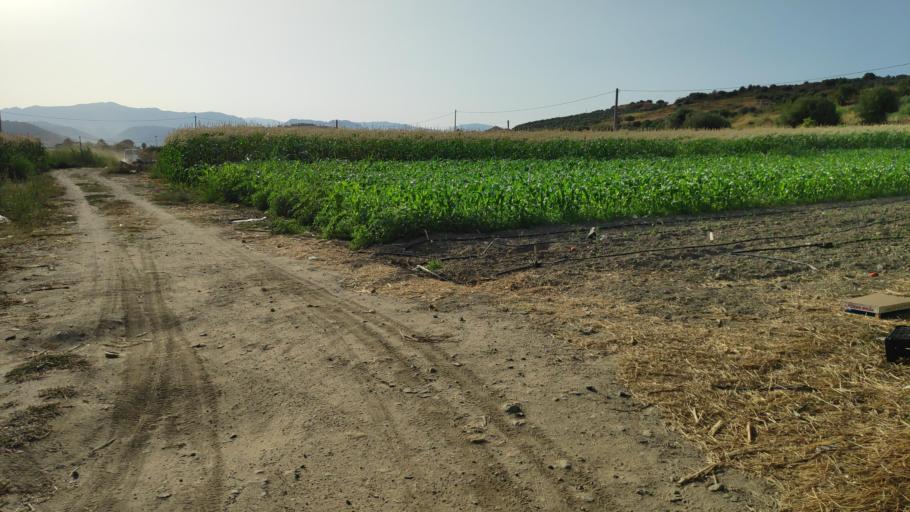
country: IT
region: Calabria
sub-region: Provincia di Reggio Calabria
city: Monasterace Marina
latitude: 38.4364
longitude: 16.5623
